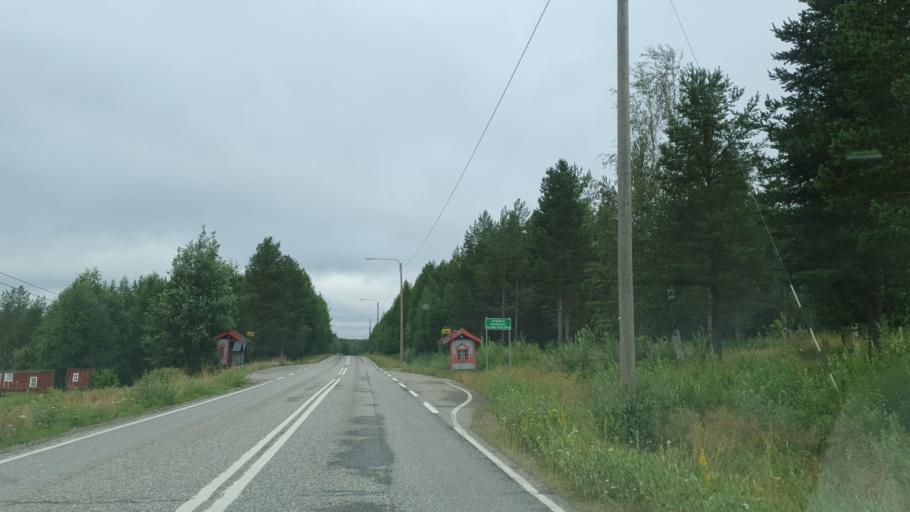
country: FI
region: Lapland
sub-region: Pohjois-Lappi
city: Sodankylae
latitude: 67.3737
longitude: 26.8844
